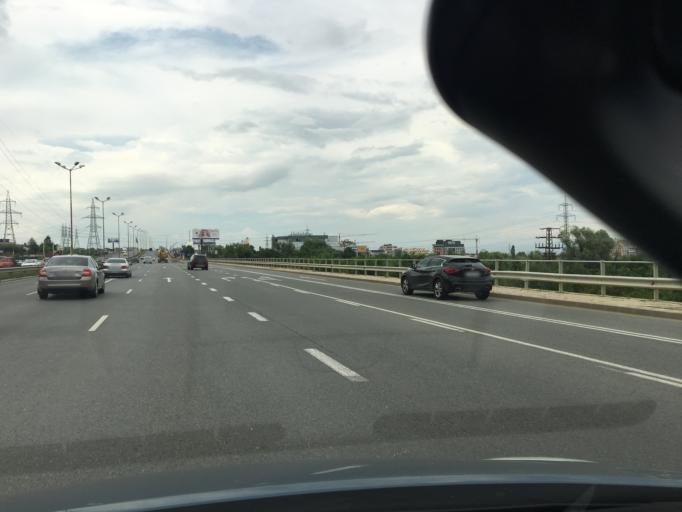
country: BG
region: Sofia-Capital
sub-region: Stolichna Obshtina
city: Sofia
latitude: 42.6308
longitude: 23.3393
